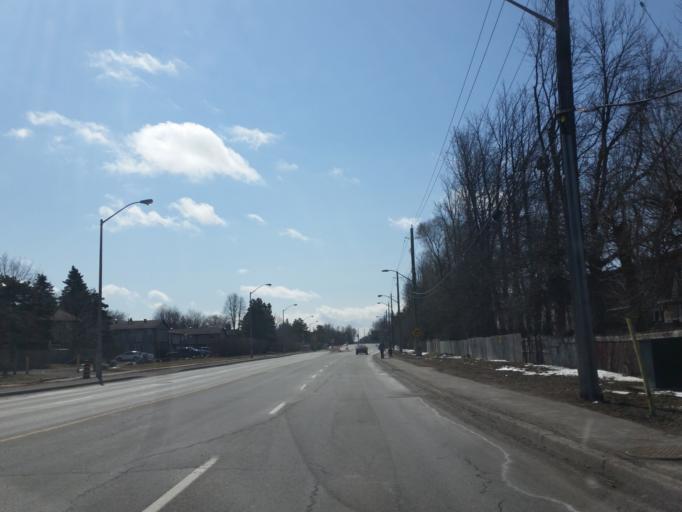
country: CA
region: Ontario
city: Bells Corners
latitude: 45.3191
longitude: -75.8315
